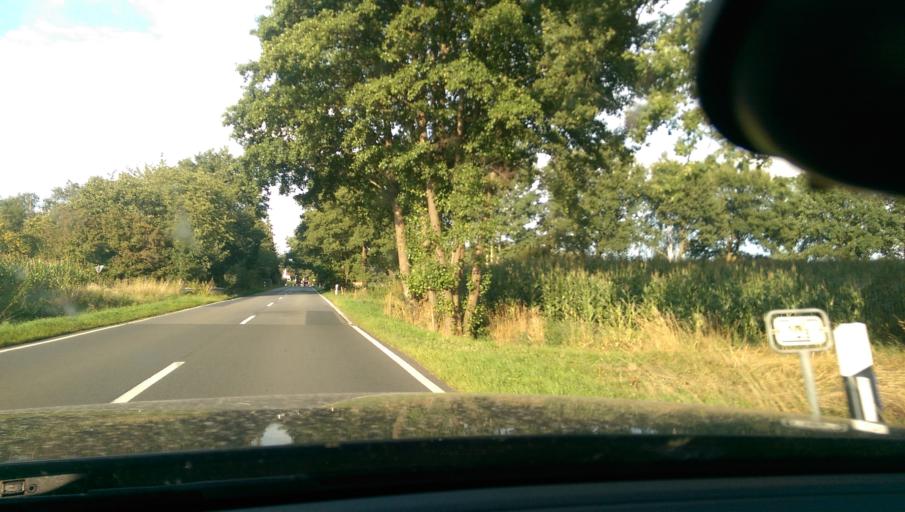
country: DE
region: Lower Saxony
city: Neustadt am Rubenberge
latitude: 52.5716
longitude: 9.5593
